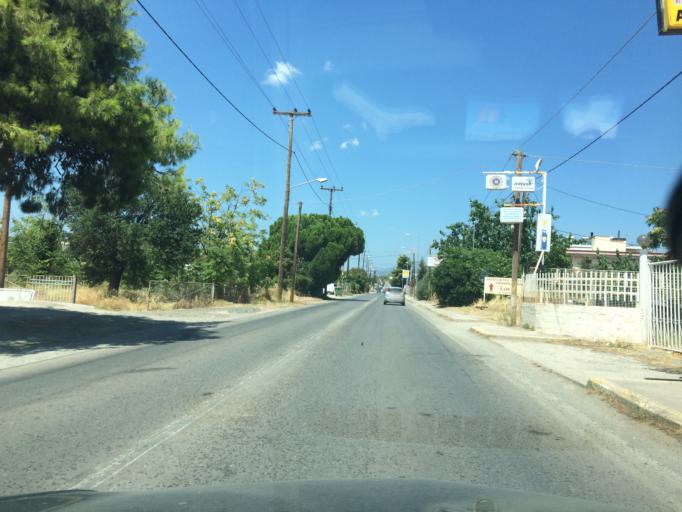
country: GR
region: Central Greece
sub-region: Nomos Evvoias
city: Nea Artaki
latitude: 38.5181
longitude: 23.6373
